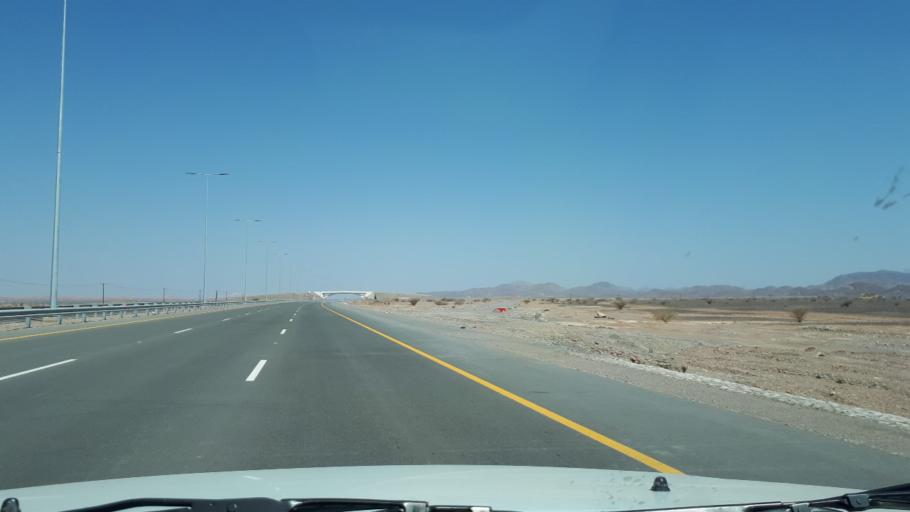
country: OM
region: Ash Sharqiyah
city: Badiyah
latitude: 22.4298
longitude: 59.0356
